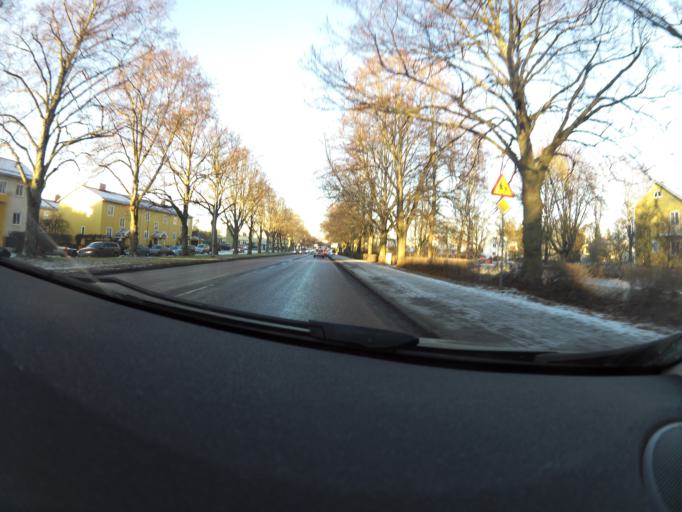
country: SE
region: Gaevleborg
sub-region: Gavle Kommun
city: Gavle
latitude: 60.6650
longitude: 17.1378
